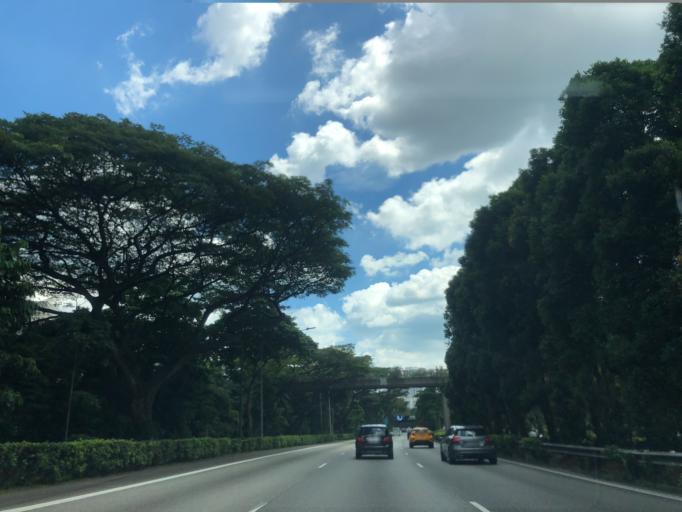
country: SG
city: Singapore
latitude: 1.2827
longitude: 103.8141
